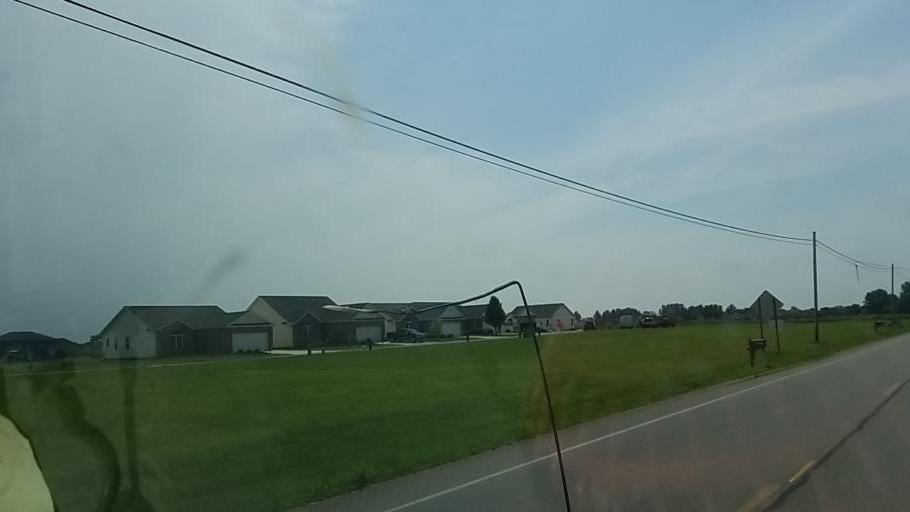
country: US
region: Ohio
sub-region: Marion County
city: Marion
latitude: 40.5949
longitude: -83.0736
